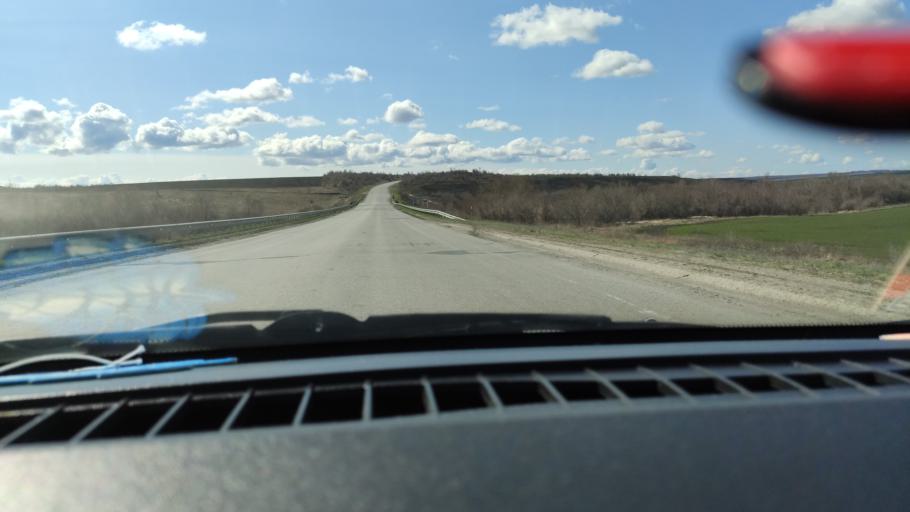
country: RU
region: Samara
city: Varlamovo
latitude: 53.0686
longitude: 48.3540
